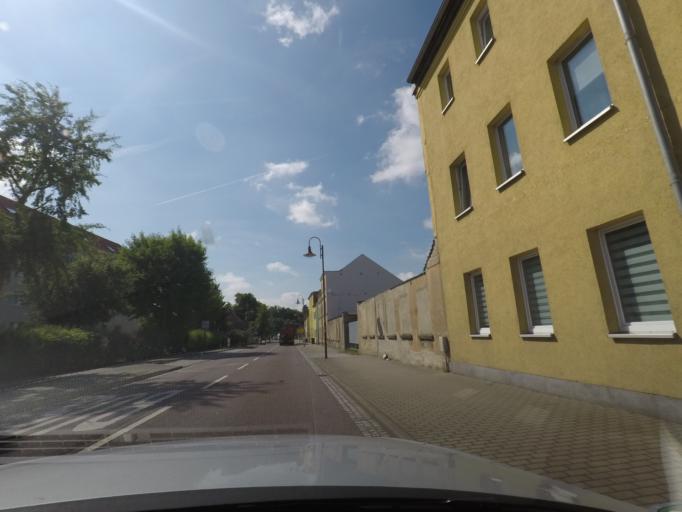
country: DE
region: Saxony
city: Markranstadt
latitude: 51.3063
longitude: 12.2162
